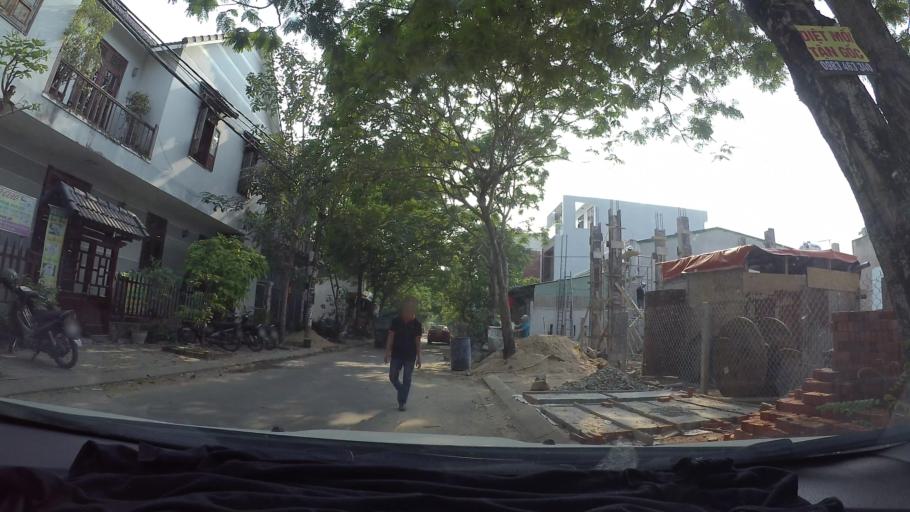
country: VN
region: Da Nang
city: Thanh Khe
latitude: 16.0479
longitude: 108.1741
